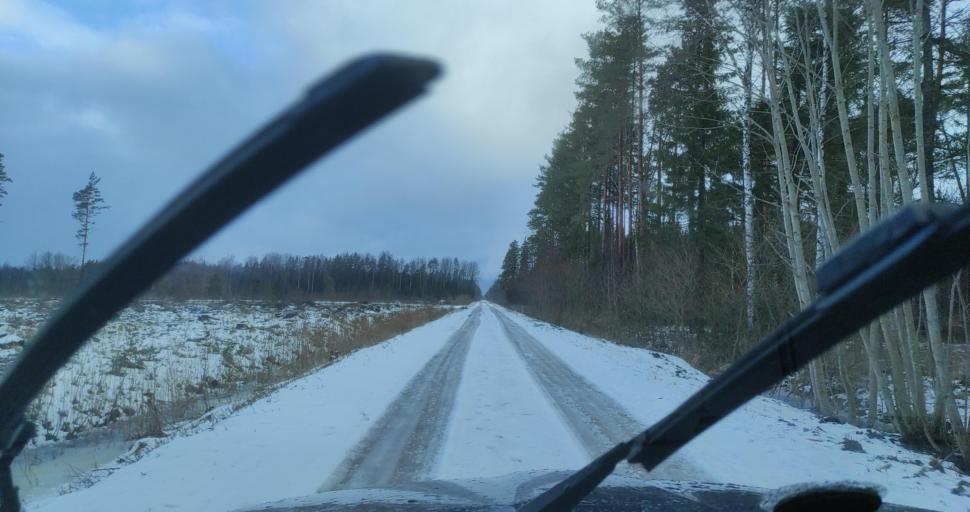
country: LV
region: Dundaga
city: Dundaga
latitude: 57.4024
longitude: 22.1029
